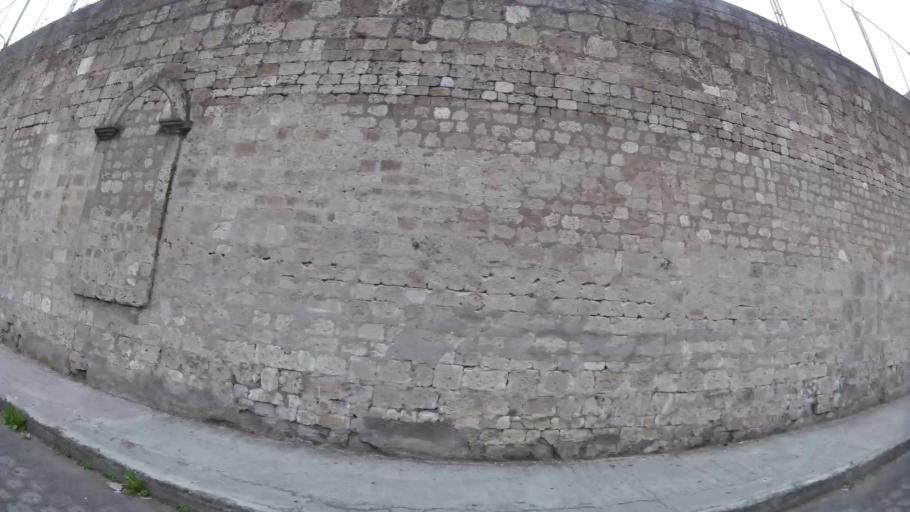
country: EC
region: Cotopaxi
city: Latacunga
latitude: -0.9368
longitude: -78.6155
